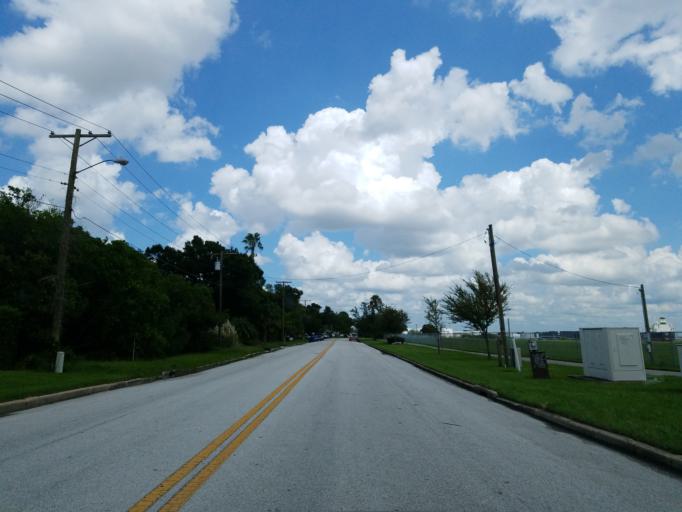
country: US
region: Florida
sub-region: Hillsborough County
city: Tampa
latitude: 27.9159
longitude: -82.4528
